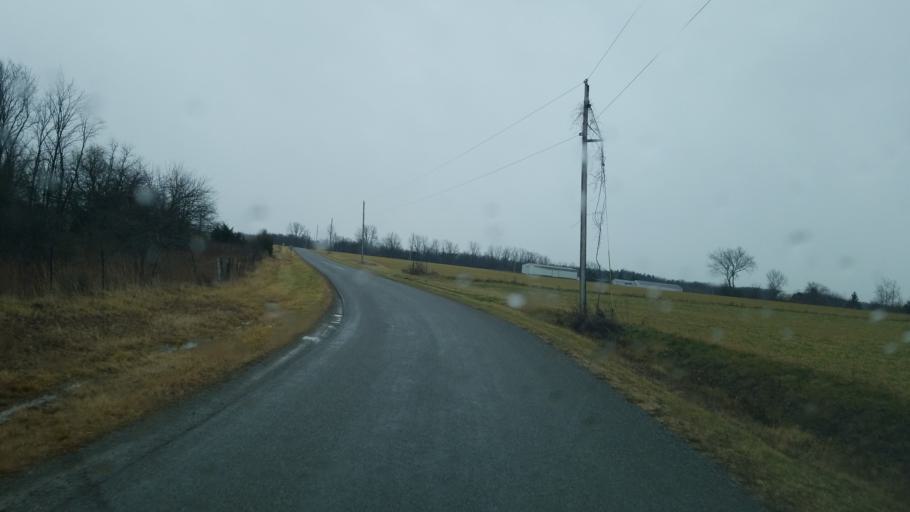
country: US
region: Ohio
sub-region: Logan County
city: Northwood
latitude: 40.4653
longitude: -83.6584
